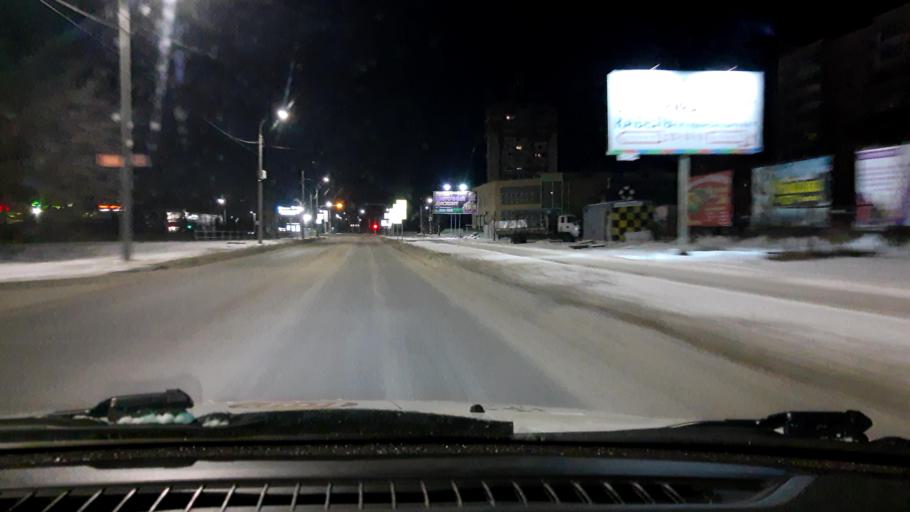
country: RU
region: Nizjnij Novgorod
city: Dzerzhinsk
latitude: 56.2298
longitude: 43.4113
